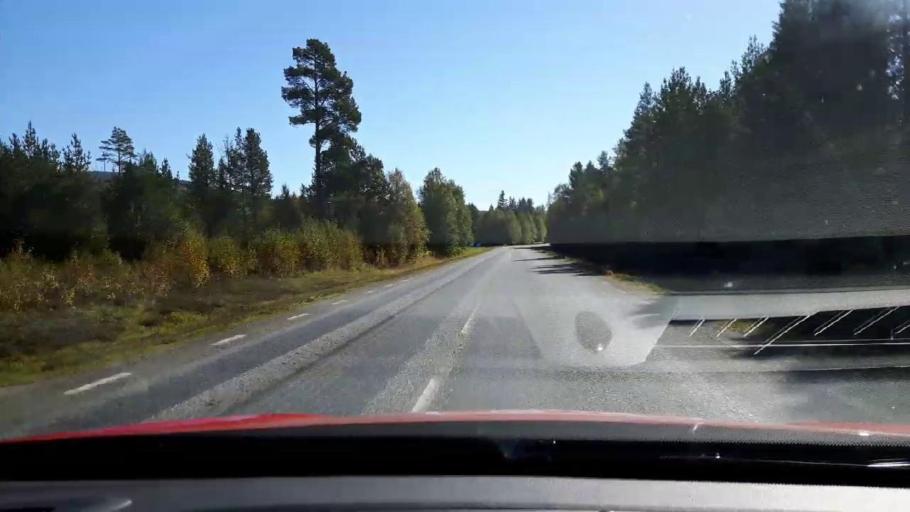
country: SE
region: Jaemtland
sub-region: Harjedalens Kommun
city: Sveg
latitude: 62.3534
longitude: 14.0244
